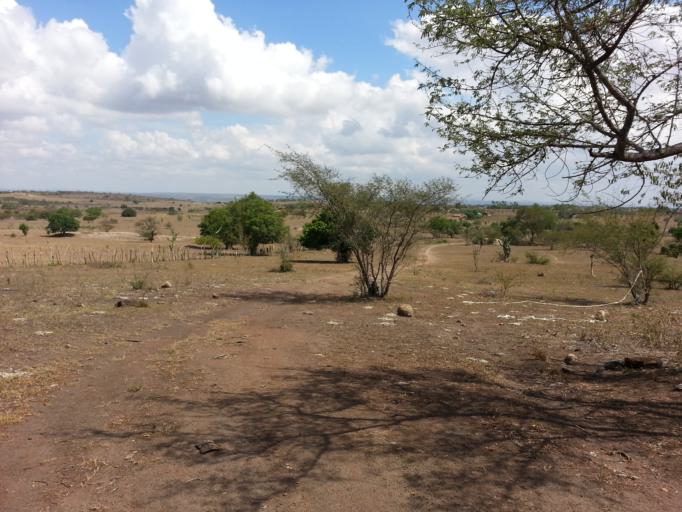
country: BR
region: Bahia
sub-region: Cruz Das Almas
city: Cruz das Almas
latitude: -12.5965
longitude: -39.1925
